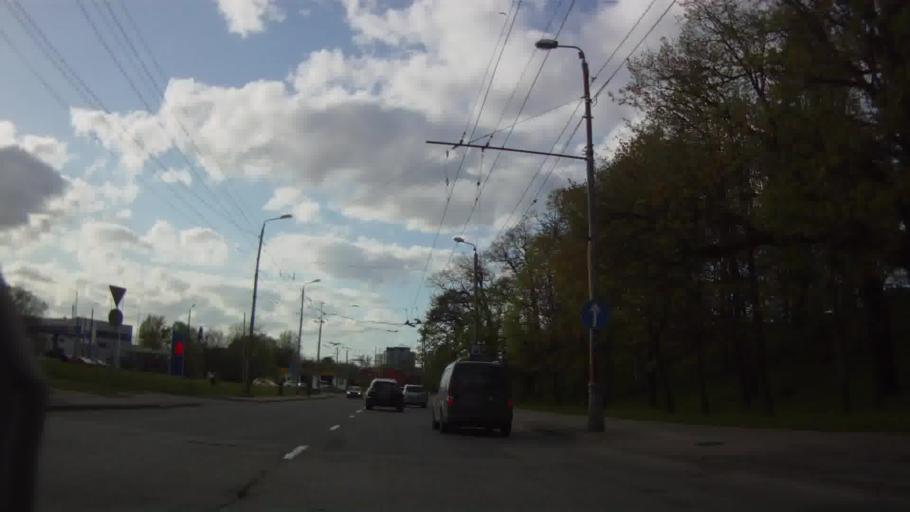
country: LV
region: Riga
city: Riga
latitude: 56.9877
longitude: 24.1318
